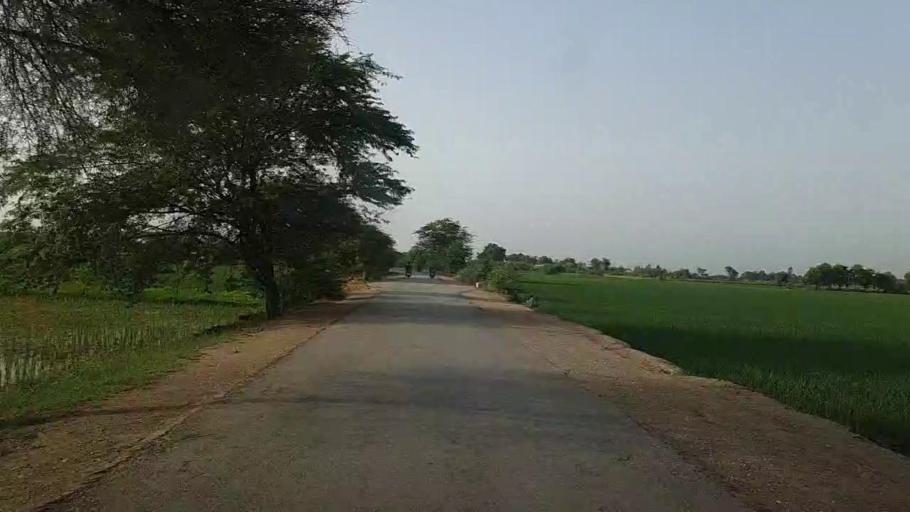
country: PK
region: Sindh
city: Mehar
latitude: 27.1351
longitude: 67.7903
